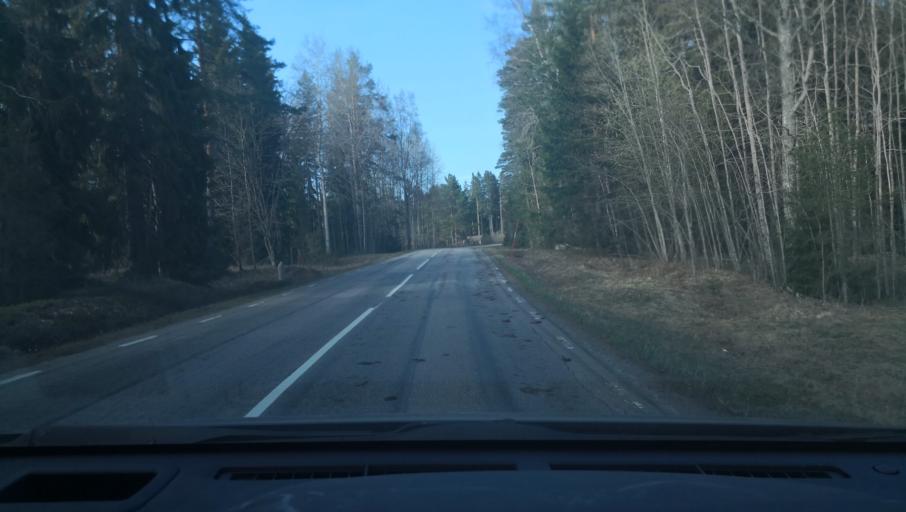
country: SE
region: Uppsala
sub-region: Heby Kommun
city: Heby
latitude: 59.9808
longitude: 16.9071
